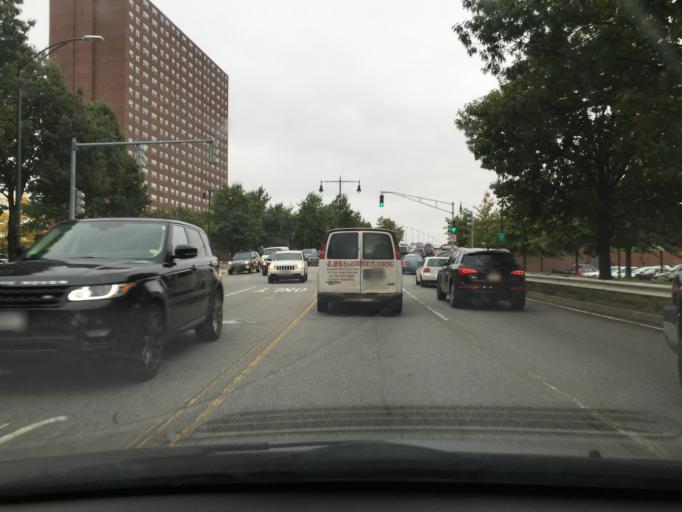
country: US
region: Massachusetts
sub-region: Middlesex County
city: Arlington
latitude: 42.3945
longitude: -71.1406
